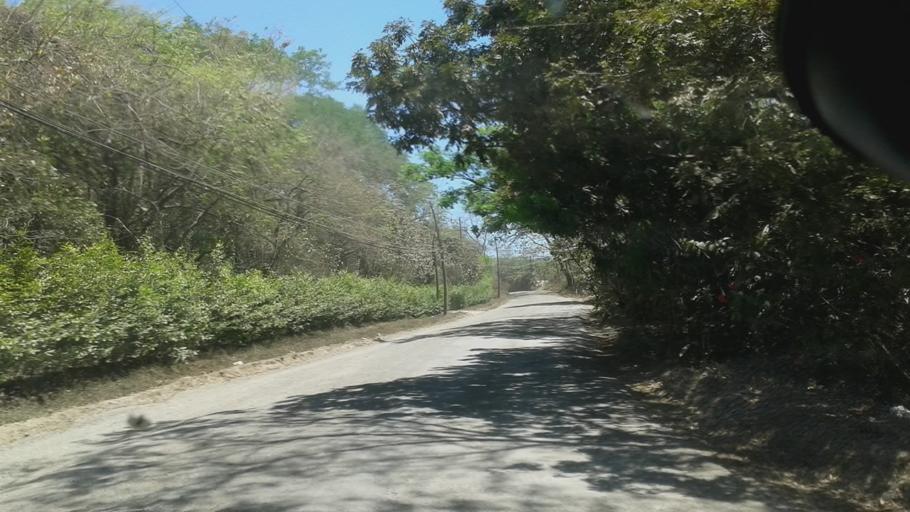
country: CR
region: Guanacaste
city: Samara
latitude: 9.9749
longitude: -85.6629
